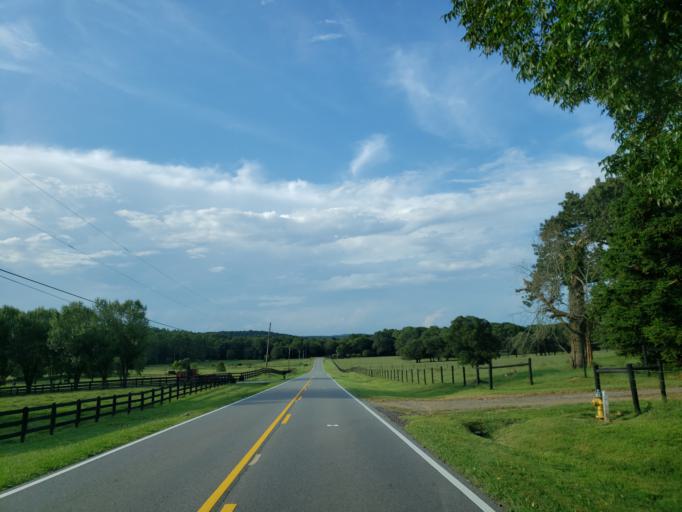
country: US
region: Georgia
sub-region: Bartow County
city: Euharlee
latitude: 34.1967
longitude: -84.9856
